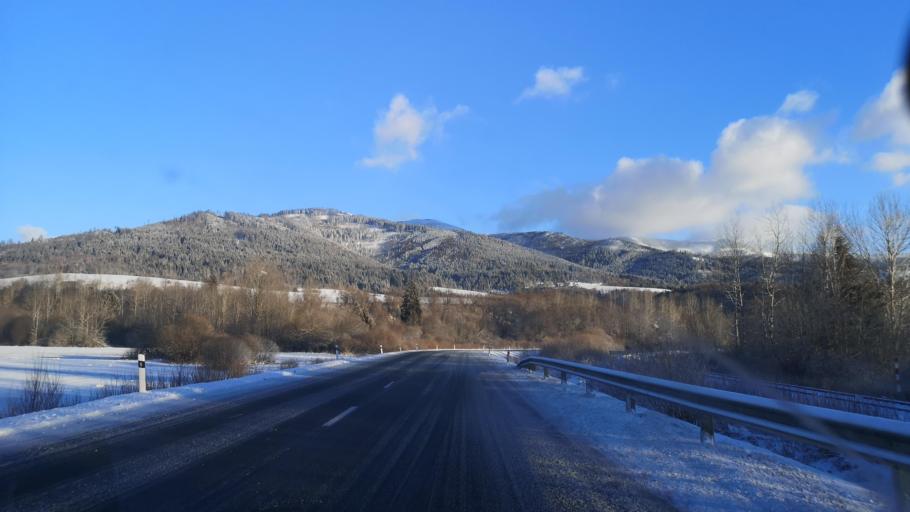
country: SK
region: Banskobystricky
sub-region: Okres Banska Bystrica
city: Brezno
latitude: 48.8495
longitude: 19.8229
